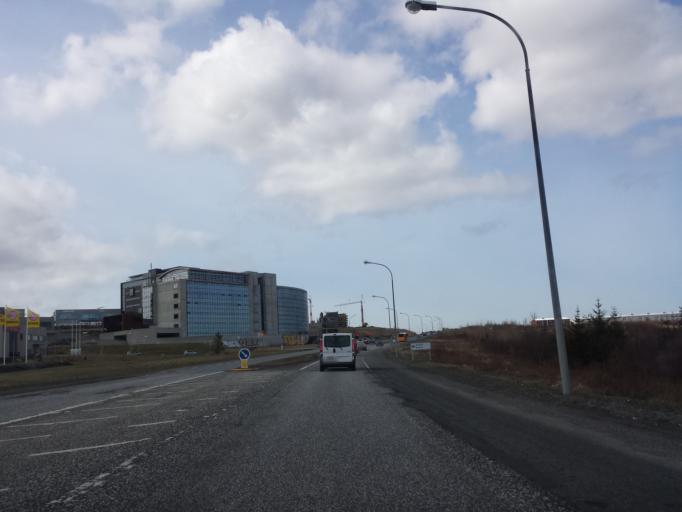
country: IS
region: Capital Region
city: Reykjavik
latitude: 64.0971
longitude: -21.8016
